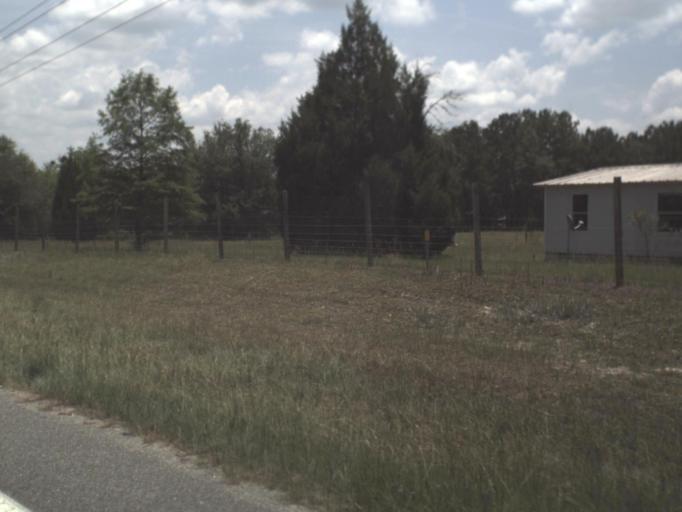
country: US
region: Florida
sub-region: Hamilton County
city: Jasper
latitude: 30.4888
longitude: -83.1684
